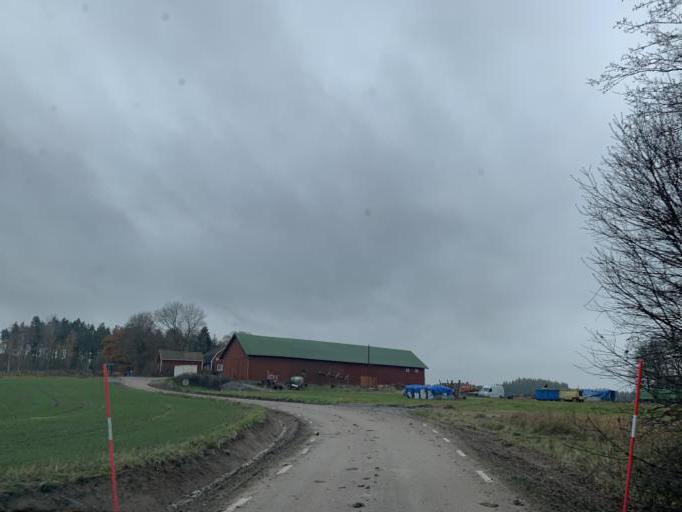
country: SE
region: Vaestmanland
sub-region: Kopings Kommun
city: Koping
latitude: 59.6341
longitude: 16.0613
